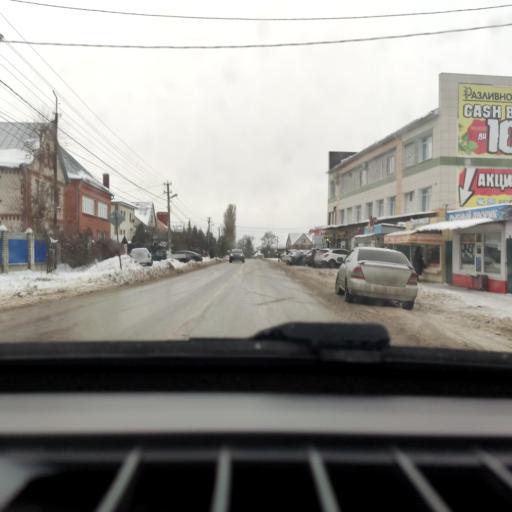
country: RU
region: Voronezj
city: Podgornoye
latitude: 51.7405
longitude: 39.1651
